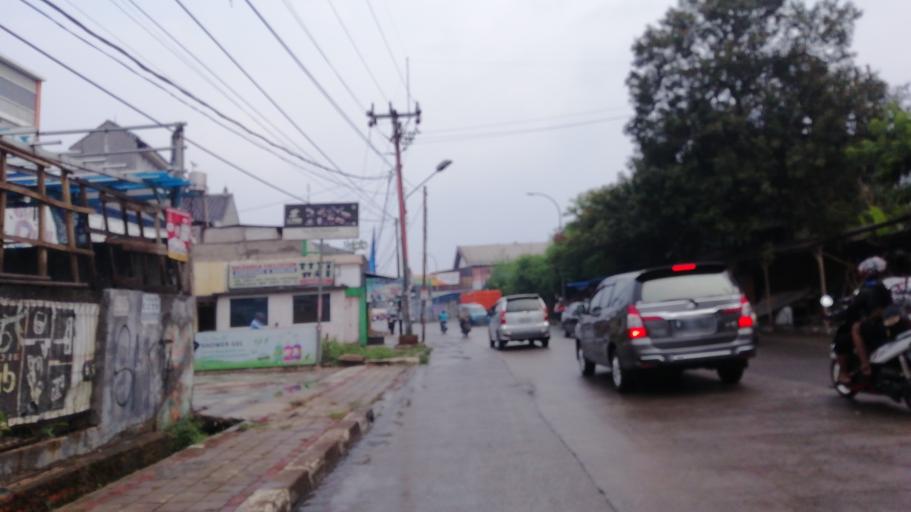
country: ID
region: West Java
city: Bogor
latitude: -6.5457
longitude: 106.8059
